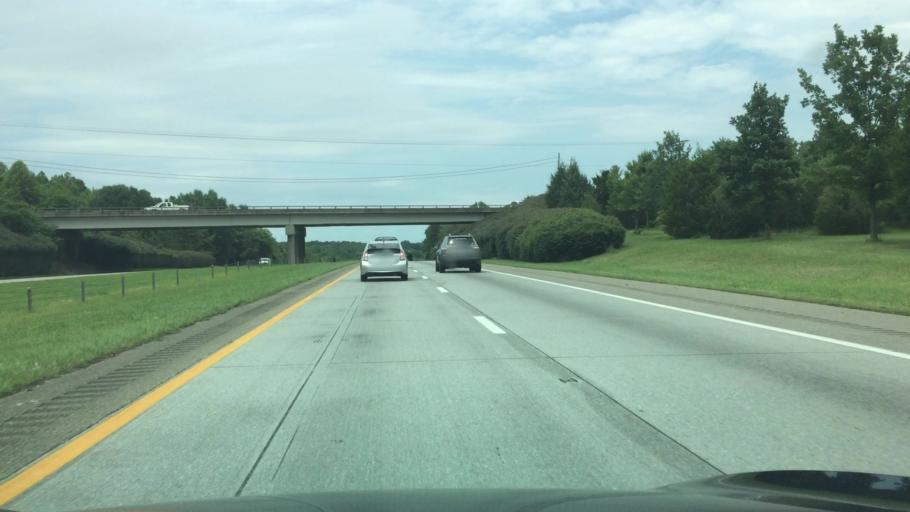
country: US
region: North Carolina
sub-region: Surry County
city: Elkin
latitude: 36.2791
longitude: -80.8223
